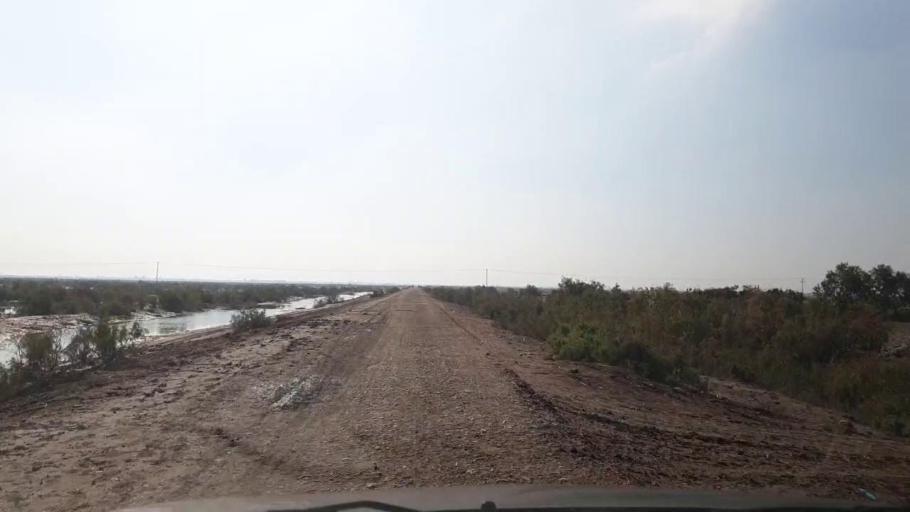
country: PK
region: Sindh
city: Sinjhoro
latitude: 26.0377
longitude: 68.7786
